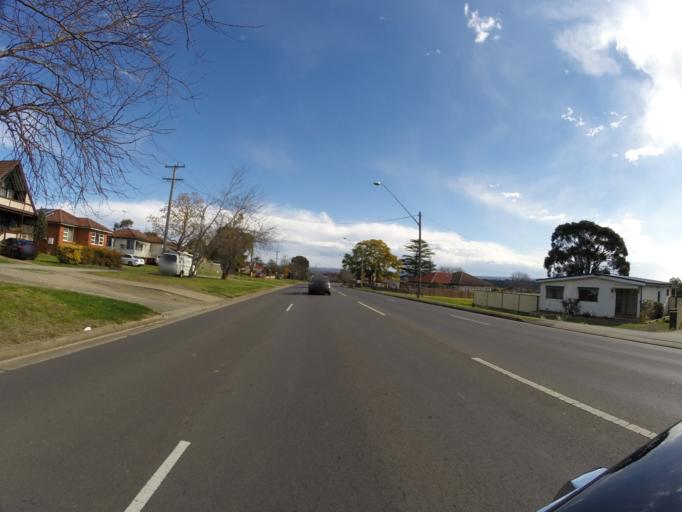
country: AU
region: New South Wales
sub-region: Camden
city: Narellan
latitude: -34.0428
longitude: 150.7286
